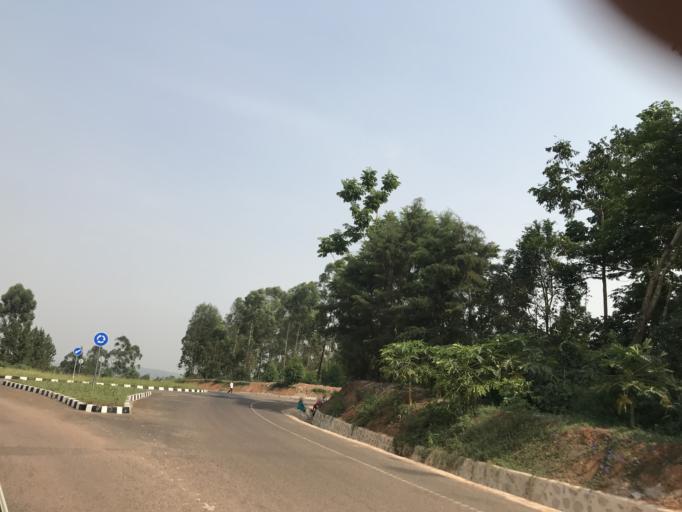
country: UG
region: Central Region
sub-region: Kalungu District
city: Kalungu
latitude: -0.2289
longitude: 31.7348
